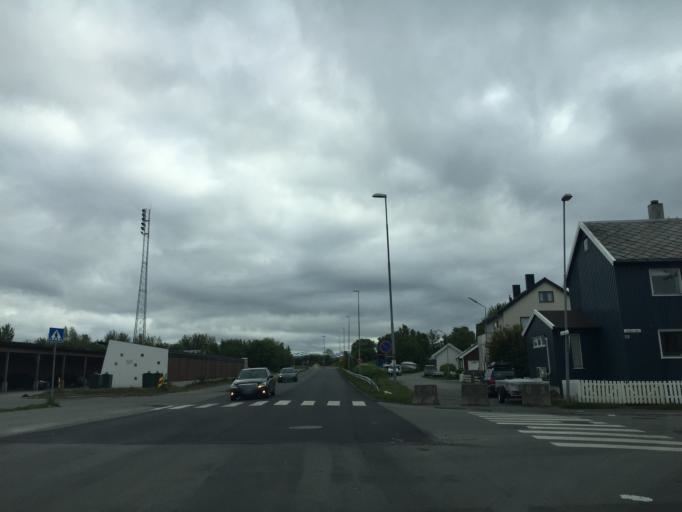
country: NO
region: Nordland
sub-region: Bodo
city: Bodo
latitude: 67.2761
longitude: 14.3823
